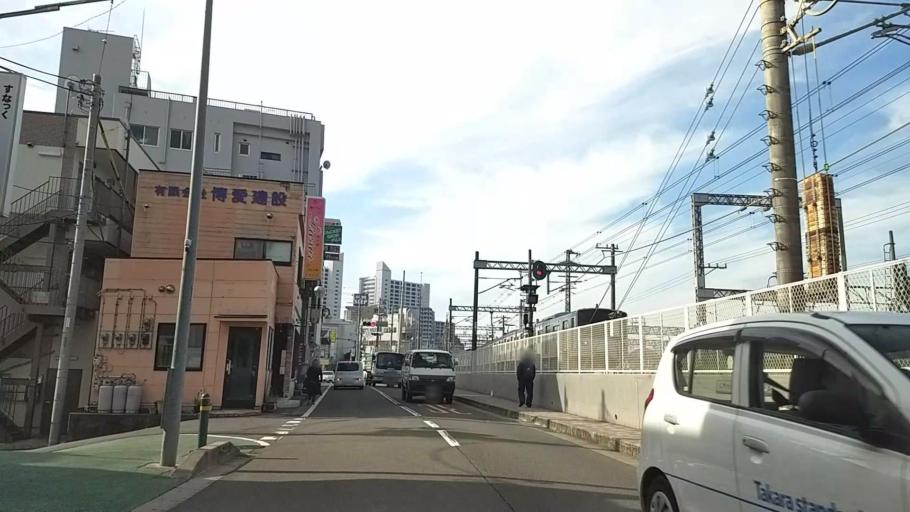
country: JP
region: Kanagawa
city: Zama
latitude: 35.4558
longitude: 139.3949
